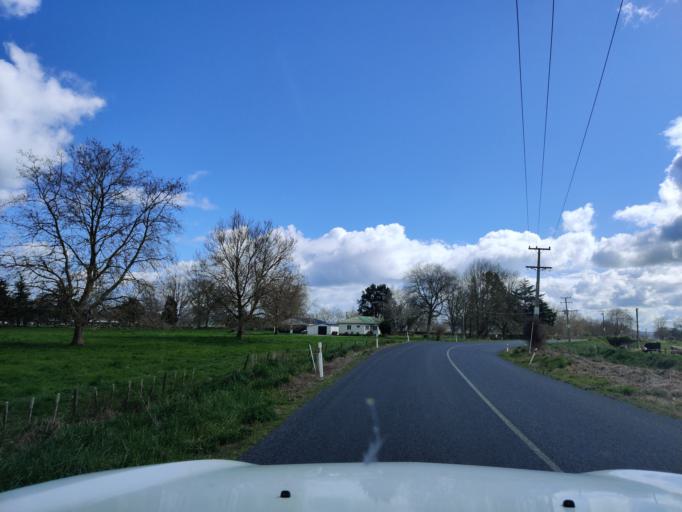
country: NZ
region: Waikato
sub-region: Waikato District
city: Ngaruawahia
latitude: -37.6165
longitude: 175.3157
